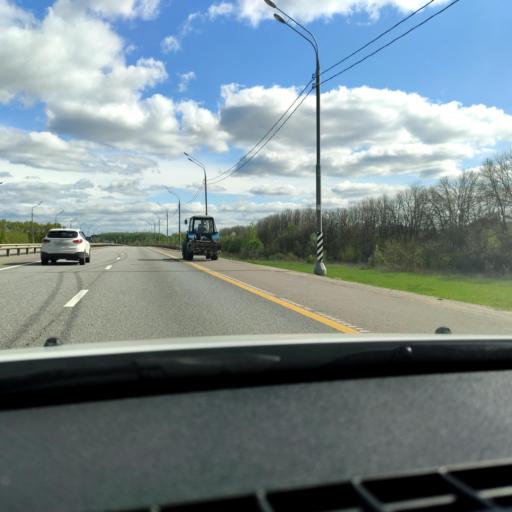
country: RU
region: Lipetsk
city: Khlevnoye
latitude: 52.2720
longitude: 39.0570
